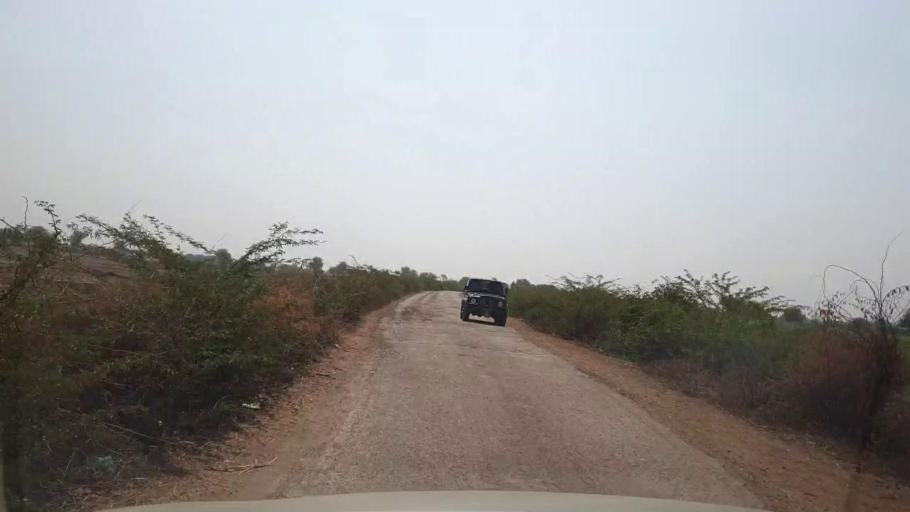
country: PK
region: Sindh
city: Dhoro Naro
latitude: 25.4708
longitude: 69.6378
